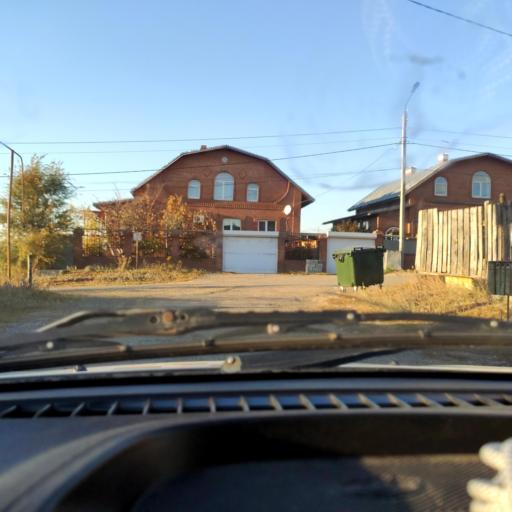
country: RU
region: Samara
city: Zhigulevsk
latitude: 53.4882
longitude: 49.5271
